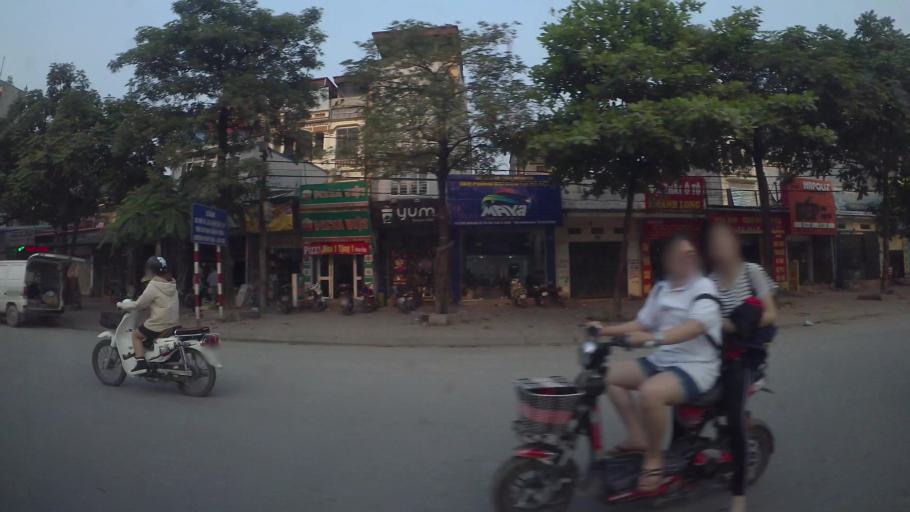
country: VN
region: Ha Noi
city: Van Dien
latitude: 20.9415
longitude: 105.8440
